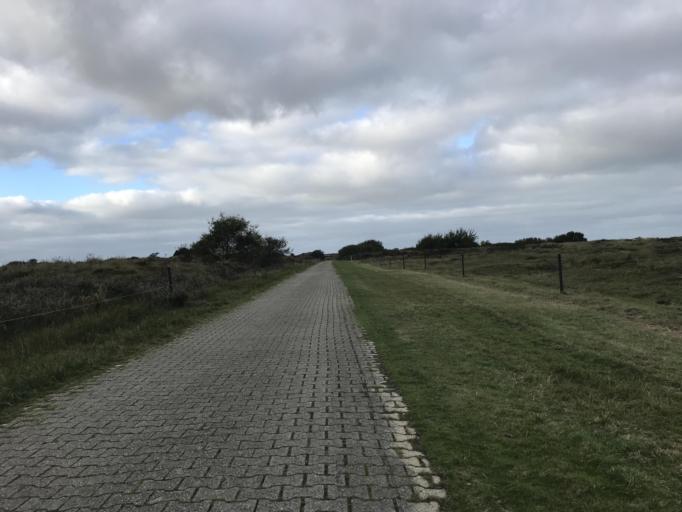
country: DE
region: Lower Saxony
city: Borkum
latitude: 53.5986
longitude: 6.7351
